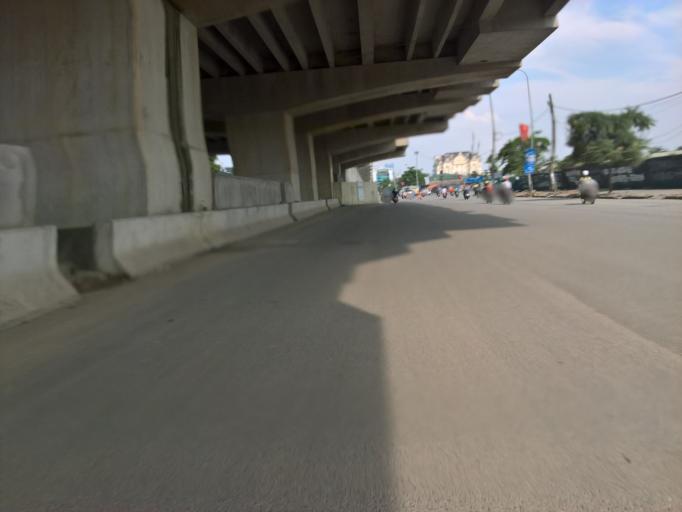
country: VN
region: Ha Noi
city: Troi
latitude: 21.0525
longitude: 105.7353
